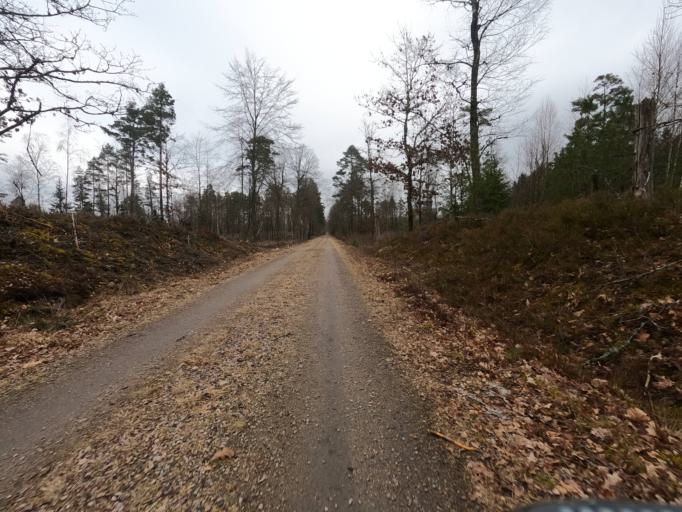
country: SE
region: Kronoberg
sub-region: Markaryds Kommun
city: Stromsnasbruk
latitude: 56.7969
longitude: 13.6718
